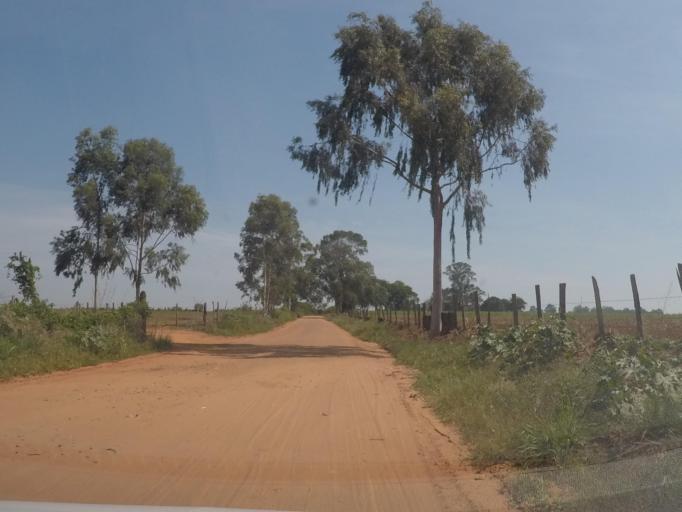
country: BR
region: Sao Paulo
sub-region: Sumare
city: Sumare
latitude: -22.8728
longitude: -47.2869
